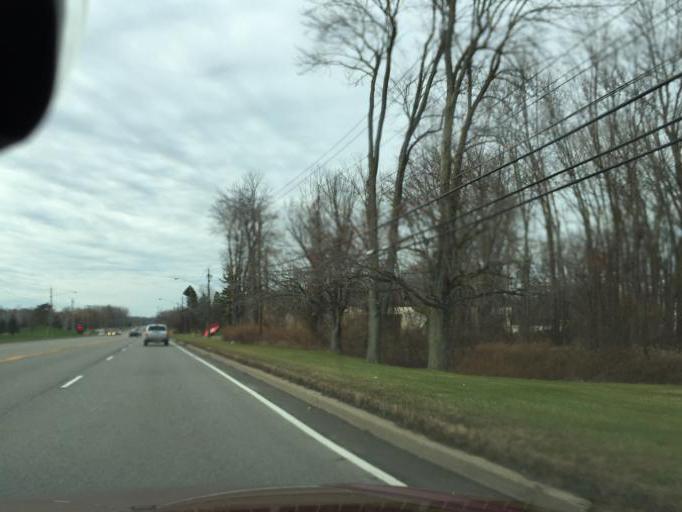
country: US
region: New York
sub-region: Monroe County
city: Rochester
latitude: 43.0929
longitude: -77.6594
